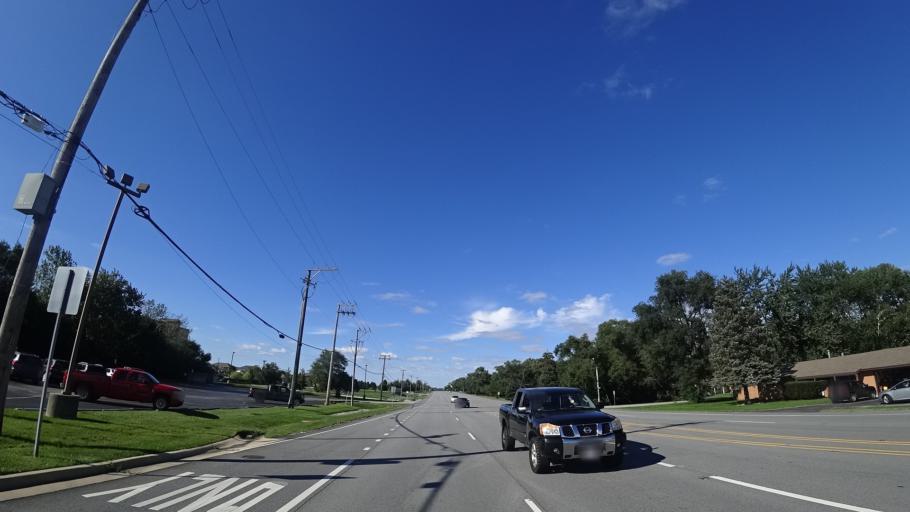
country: US
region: Illinois
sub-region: Cook County
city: Country Club Hills
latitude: 41.5578
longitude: -87.7333
